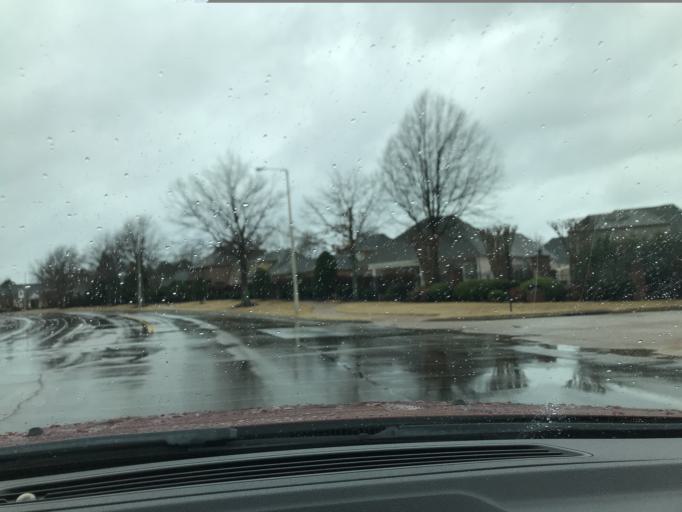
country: US
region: Tennessee
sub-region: Shelby County
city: Collierville
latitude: 35.0539
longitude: -89.6917
